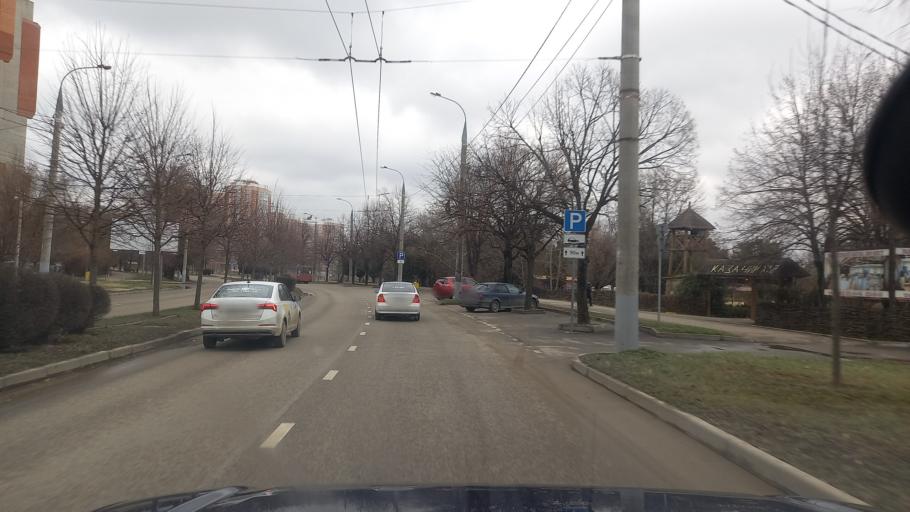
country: RU
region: Krasnodarskiy
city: Pashkovskiy
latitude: 45.0334
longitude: 39.1009
